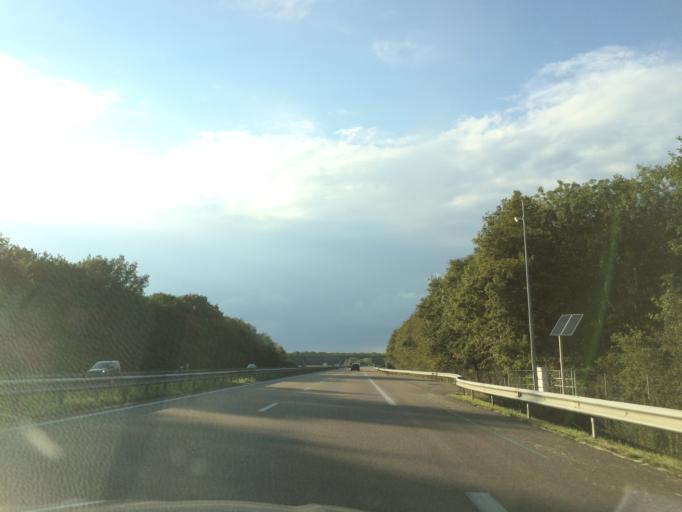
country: FR
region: Bourgogne
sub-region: Departement de l'Yonne
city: Cheroy
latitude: 48.1131
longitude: 2.9940
